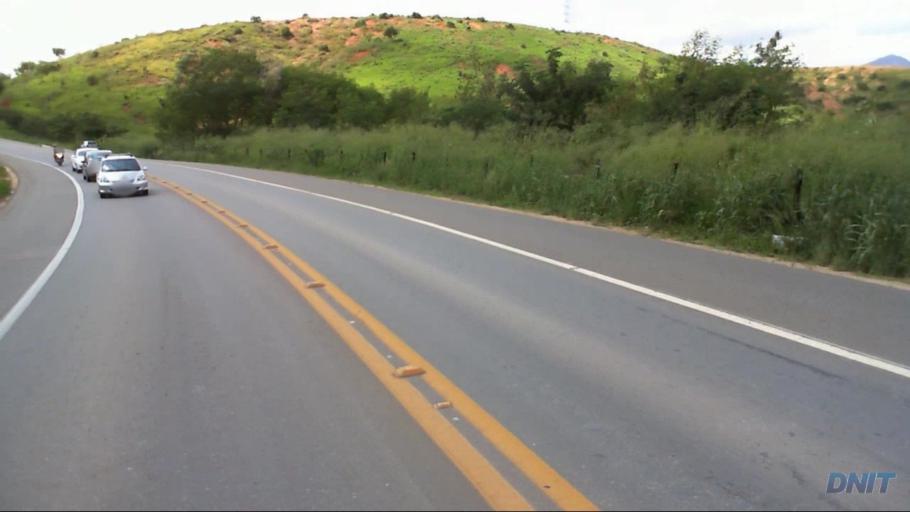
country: BR
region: Minas Gerais
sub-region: Governador Valadares
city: Governador Valadares
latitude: -18.8458
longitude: -41.9762
